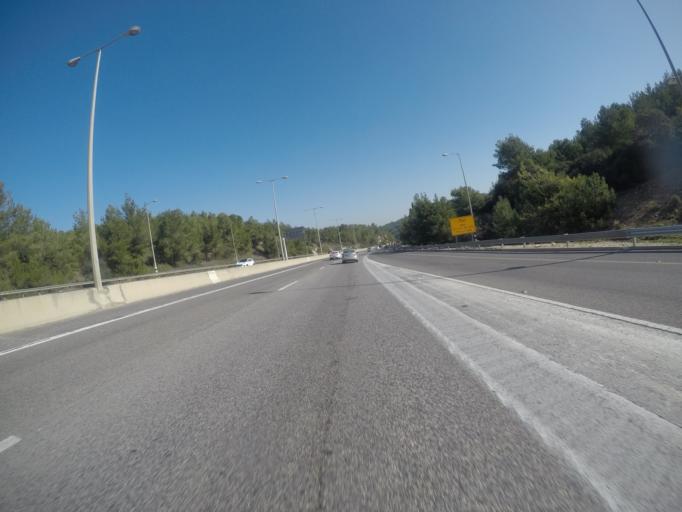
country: IL
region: Haifa
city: Daliyat el Karmil
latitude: 32.6399
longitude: 35.0683
